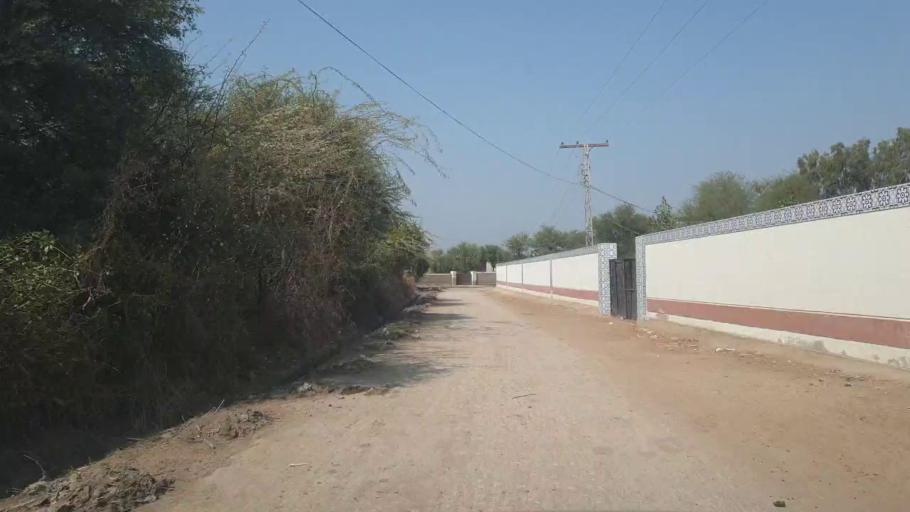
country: PK
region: Sindh
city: Tando Allahyar
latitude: 25.4313
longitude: 68.8370
